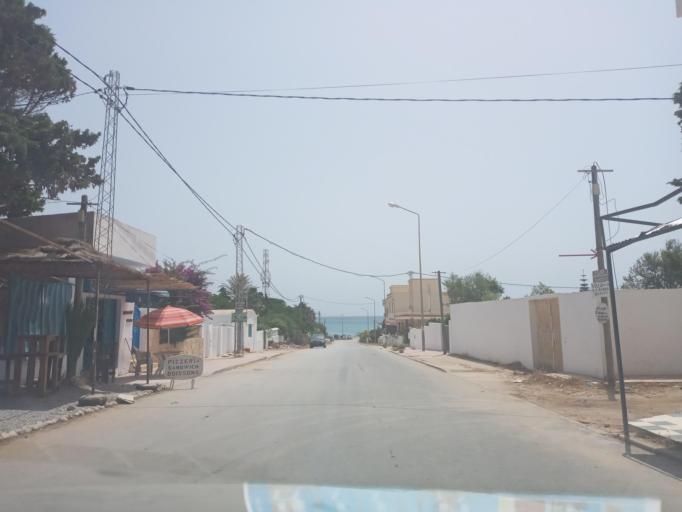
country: TN
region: Nabul
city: El Haouaria
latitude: 37.0361
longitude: 11.0562
